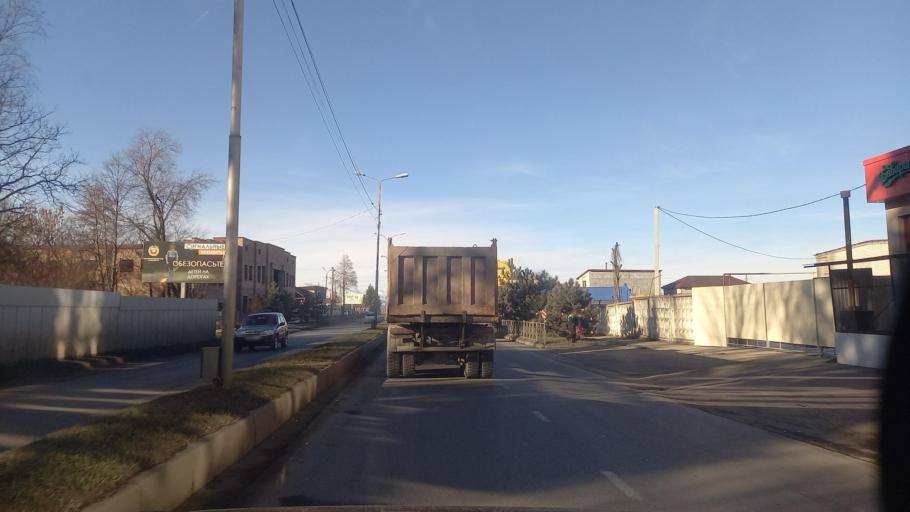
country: RU
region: North Ossetia
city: Vladikavkaz
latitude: 43.0255
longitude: 44.6402
